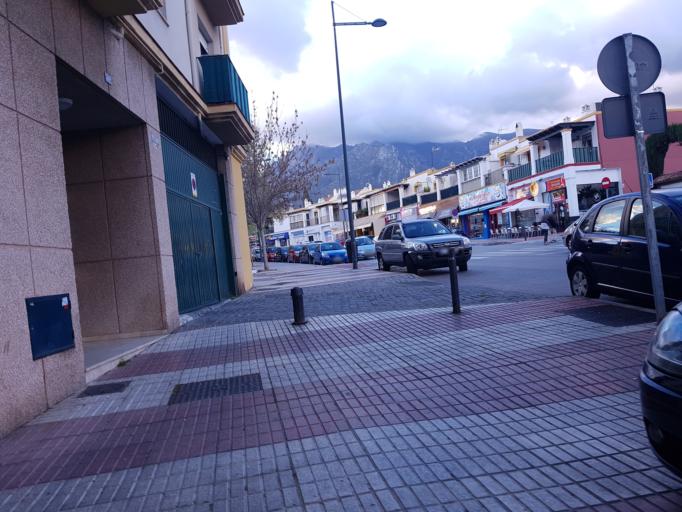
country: ES
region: Andalusia
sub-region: Provincia de Malaga
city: Marbella
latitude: 36.5174
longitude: -4.8885
